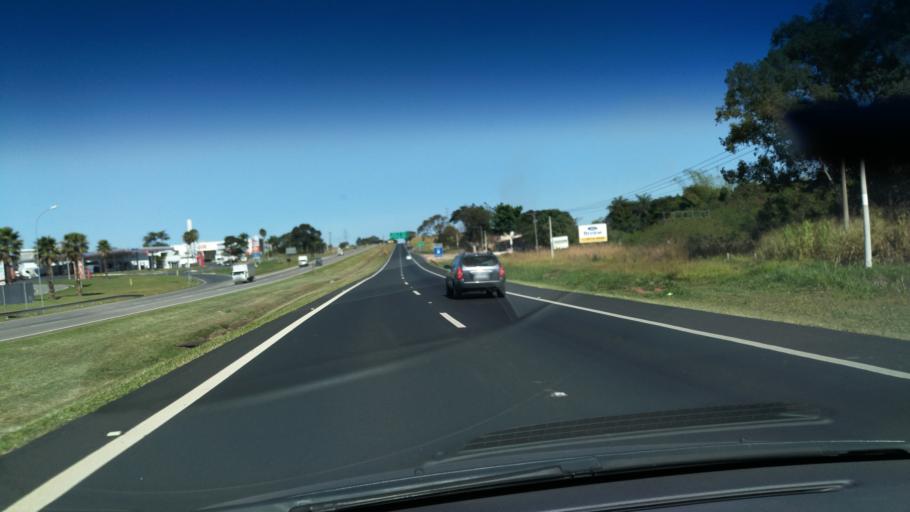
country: BR
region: Sao Paulo
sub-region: Mogi-Mirim
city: Mogi Mirim
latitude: -22.4506
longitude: -46.9828
